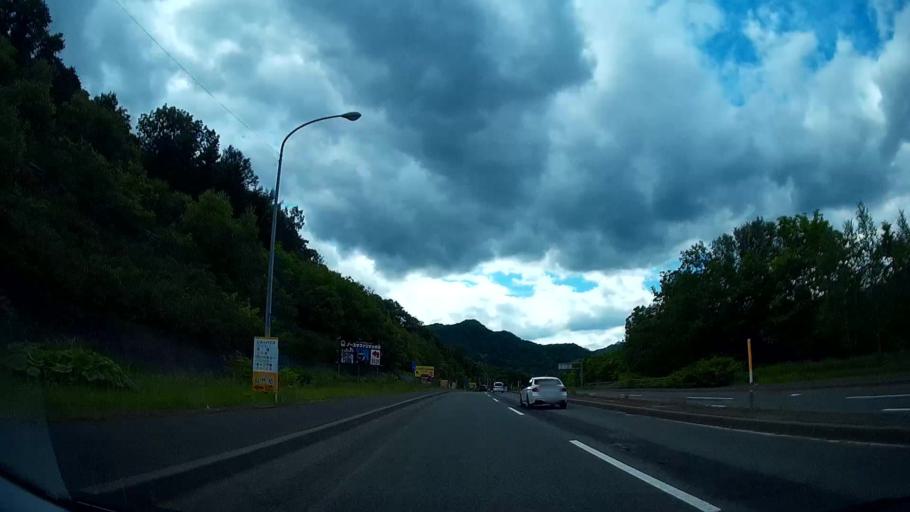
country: JP
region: Hokkaido
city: Sapporo
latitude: 42.9570
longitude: 141.2334
